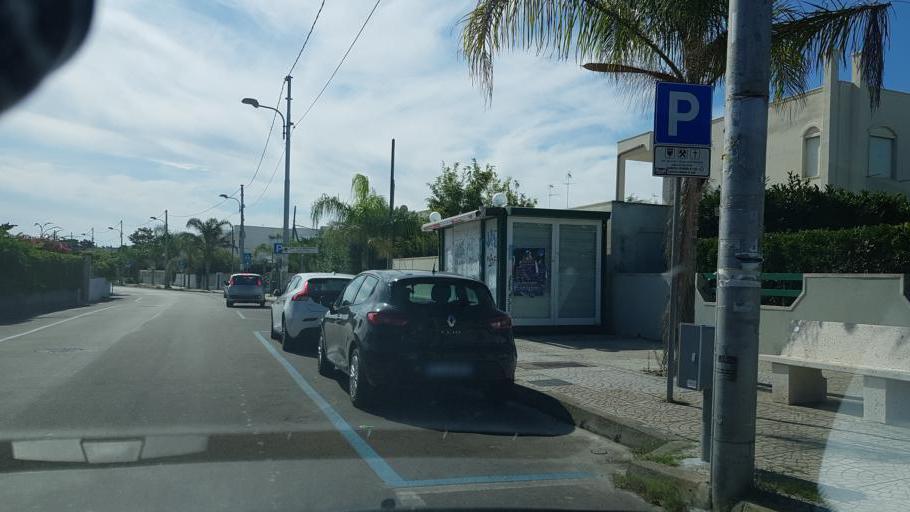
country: IT
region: Apulia
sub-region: Provincia di Lecce
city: Borgagne
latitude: 40.2730
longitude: 18.4283
